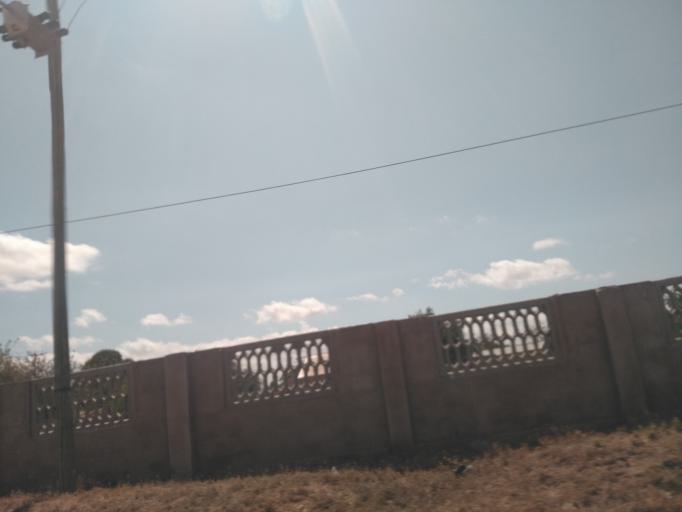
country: TZ
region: Dodoma
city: Dodoma
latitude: -6.1638
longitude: 35.7611
